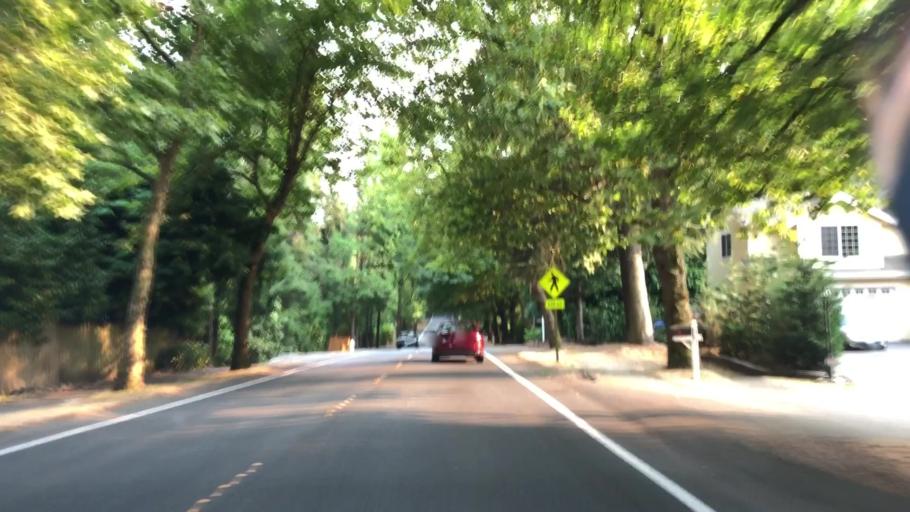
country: US
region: Washington
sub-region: King County
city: Mercer Island
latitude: 47.5474
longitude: -122.2216
